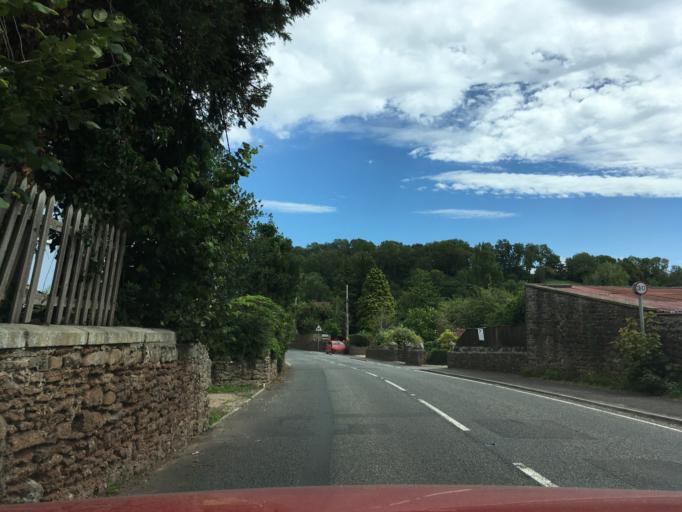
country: GB
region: England
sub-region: Somerset
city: Bradley Cross
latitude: 51.2487
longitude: -2.7390
